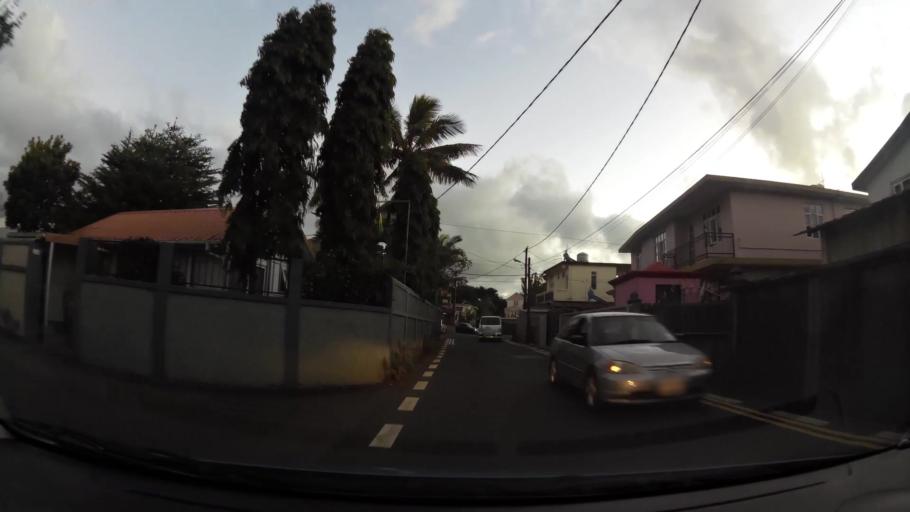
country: MU
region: Plaines Wilhems
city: Curepipe
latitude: -20.2929
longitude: 57.5201
